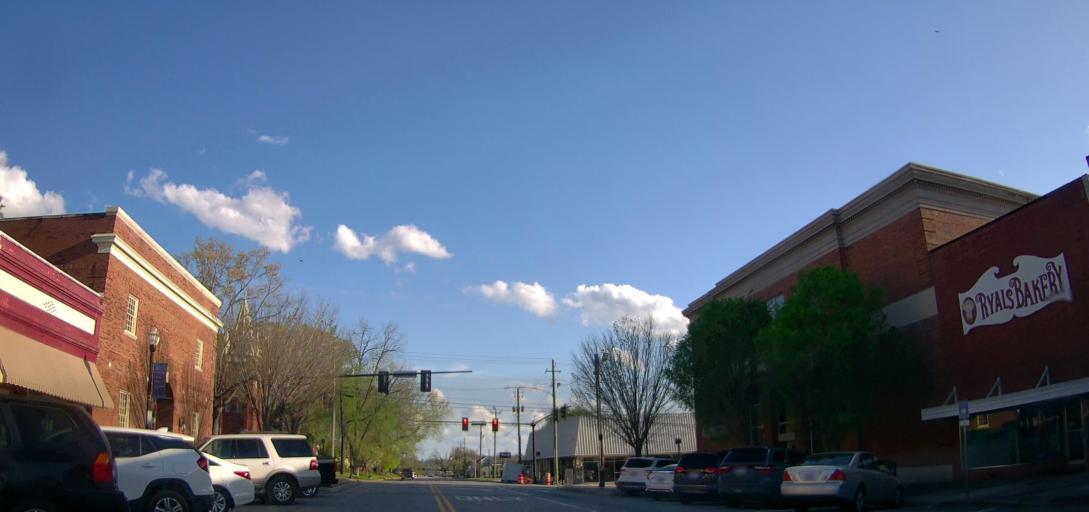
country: US
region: Georgia
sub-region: Baldwin County
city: Milledgeville
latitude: 33.0804
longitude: -83.2268
